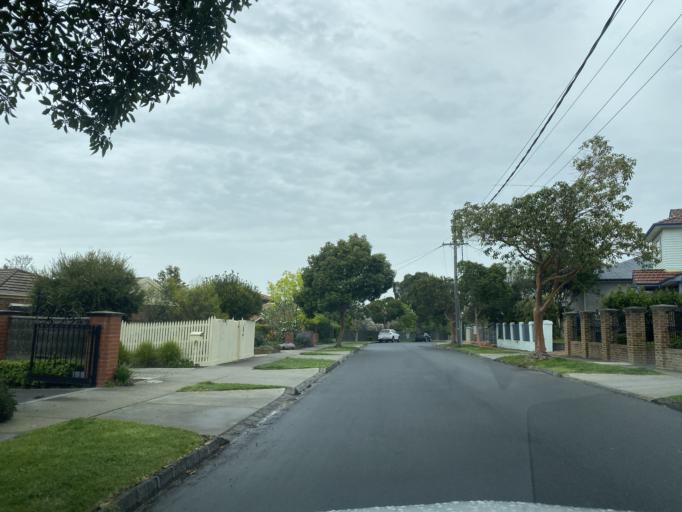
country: AU
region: Victoria
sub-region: Boroondara
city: Canterbury
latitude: -37.8391
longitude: 145.0863
